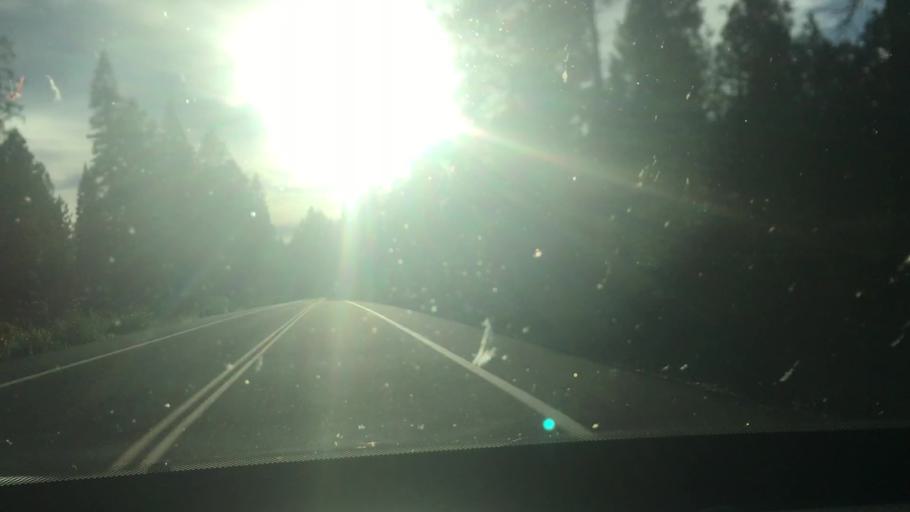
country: US
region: Oregon
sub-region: Deschutes County
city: Deschutes River Woods
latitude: 44.0403
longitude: -121.4679
